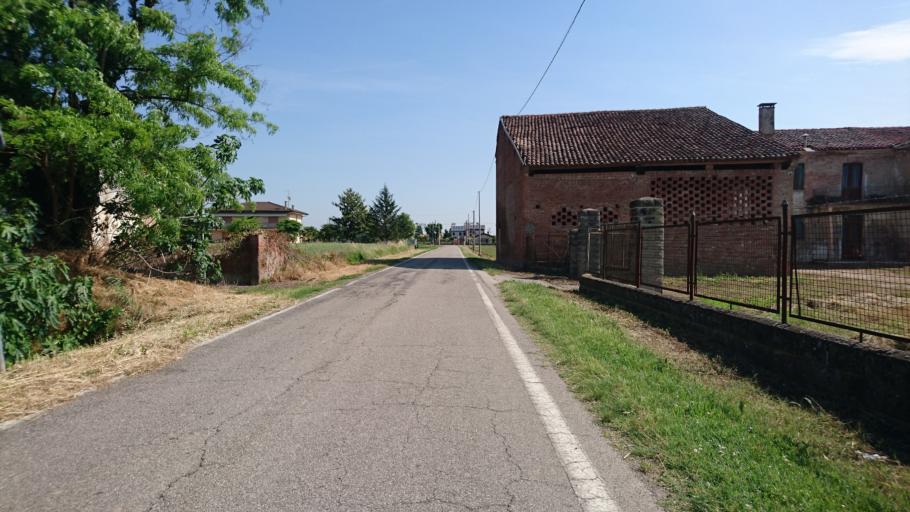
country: IT
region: Veneto
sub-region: Provincia di Padova
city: Casale di Scodosia
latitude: 45.1751
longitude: 11.4658
